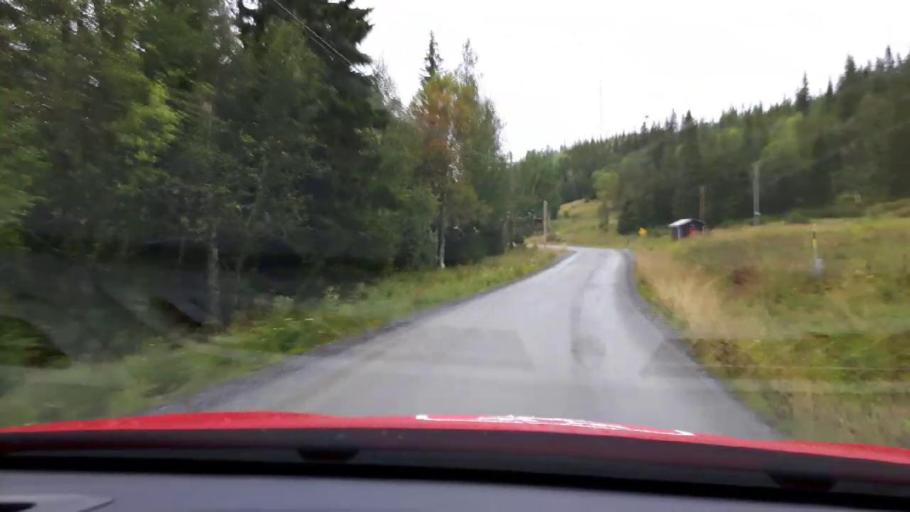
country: SE
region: Jaemtland
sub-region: Are Kommun
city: Are
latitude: 63.5082
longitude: 12.7263
